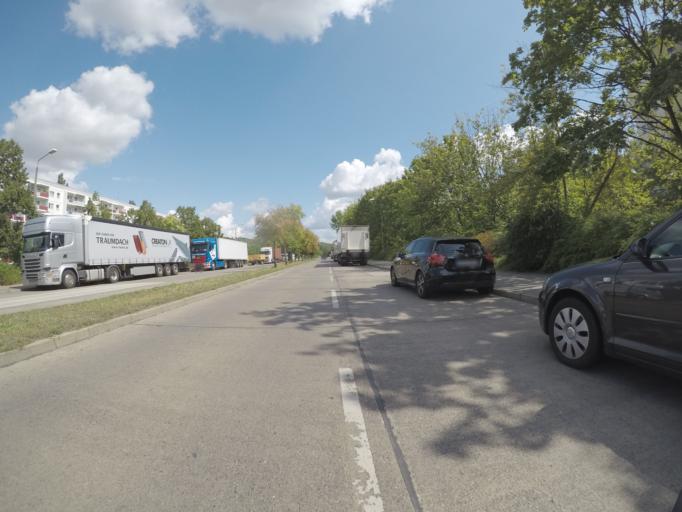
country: DE
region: Berlin
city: Marzahn
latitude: 52.5555
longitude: 13.5713
